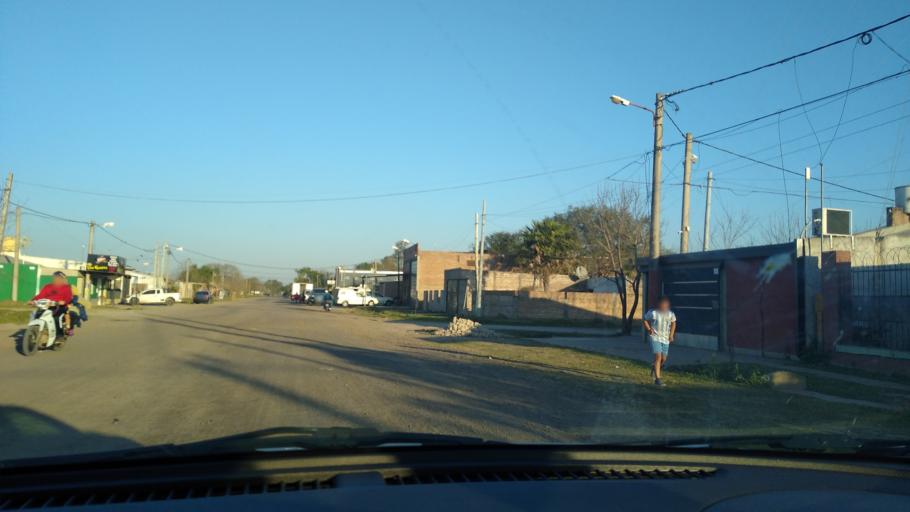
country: AR
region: Chaco
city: Puerto Vilelas
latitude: -27.4988
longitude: -58.9615
